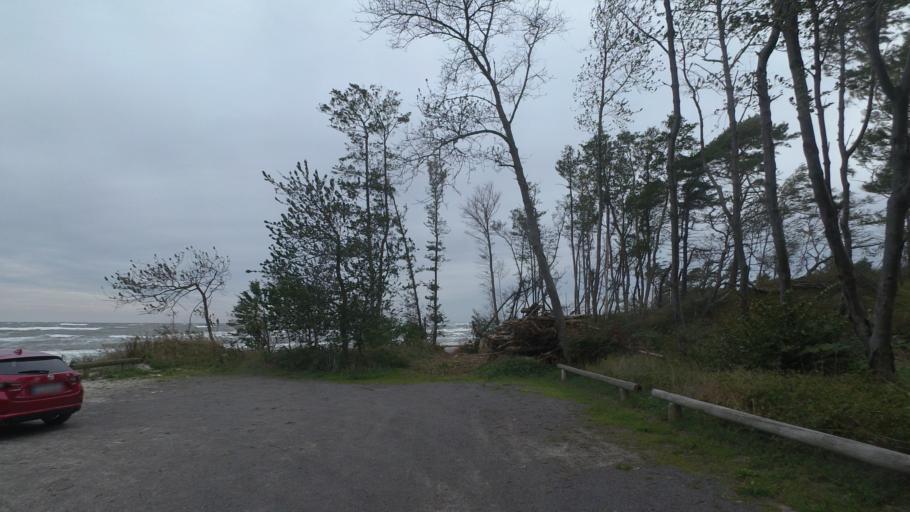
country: DK
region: Capital Region
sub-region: Bornholm Kommune
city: Nexo
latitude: 54.9956
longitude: 15.0379
